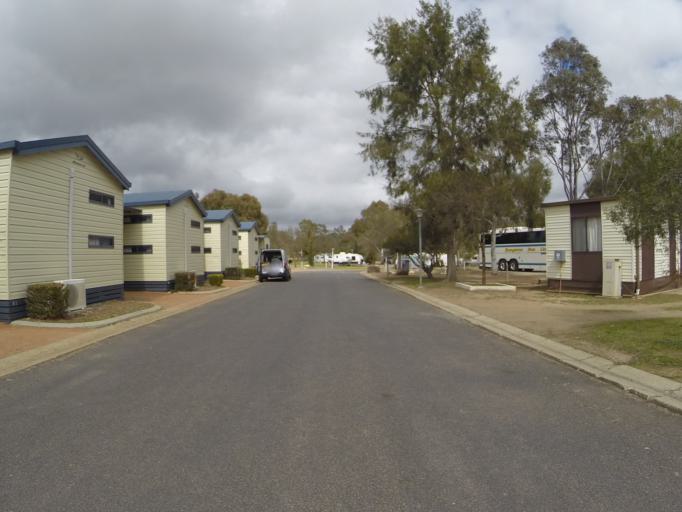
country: AU
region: Australian Capital Territory
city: Kaleen
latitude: -35.1980
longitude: 149.2271
